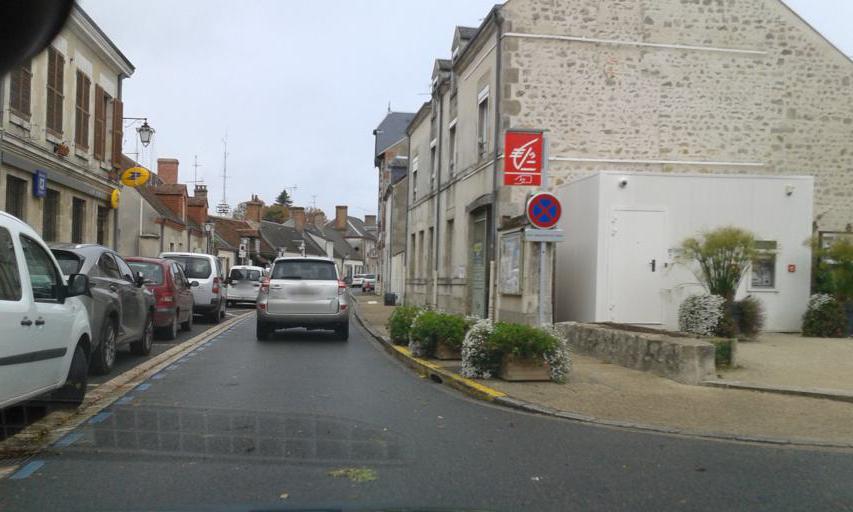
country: FR
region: Centre
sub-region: Departement du Loiret
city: Vitry-aux-Loges
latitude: 47.9390
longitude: 2.2666
